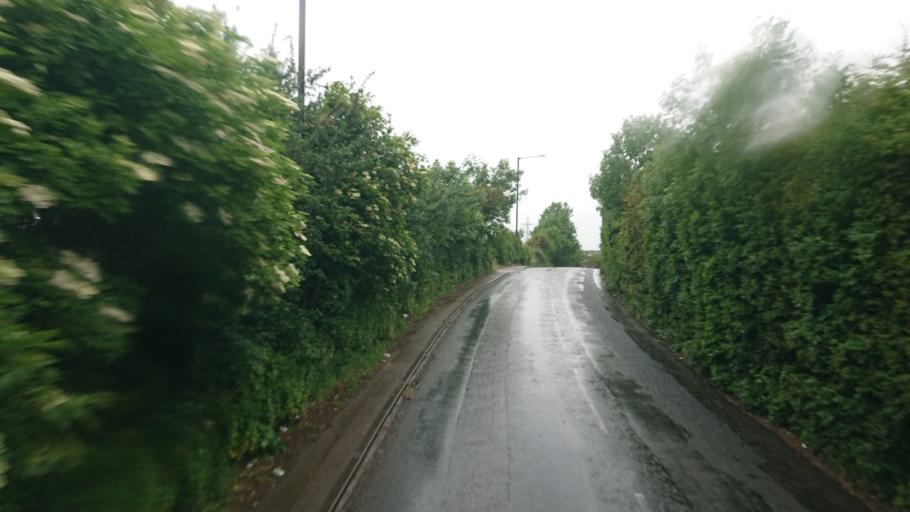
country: GB
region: England
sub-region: Lancashire
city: Morecambe
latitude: 54.0265
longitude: -2.8870
